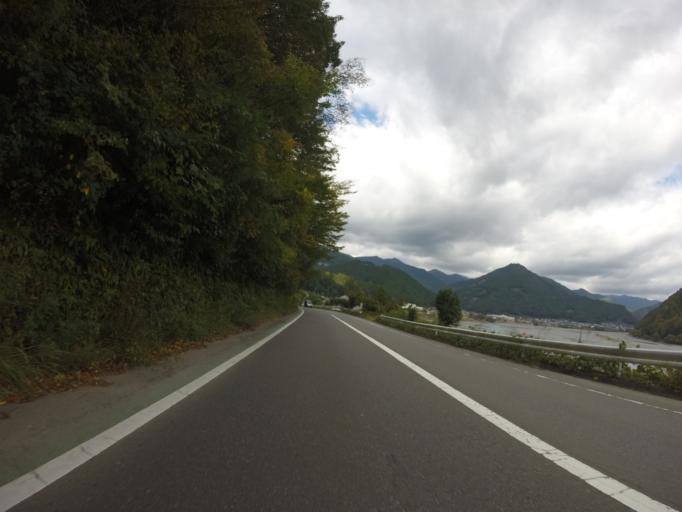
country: JP
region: Shizuoka
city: Kanaya
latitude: 35.0320
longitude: 138.0865
